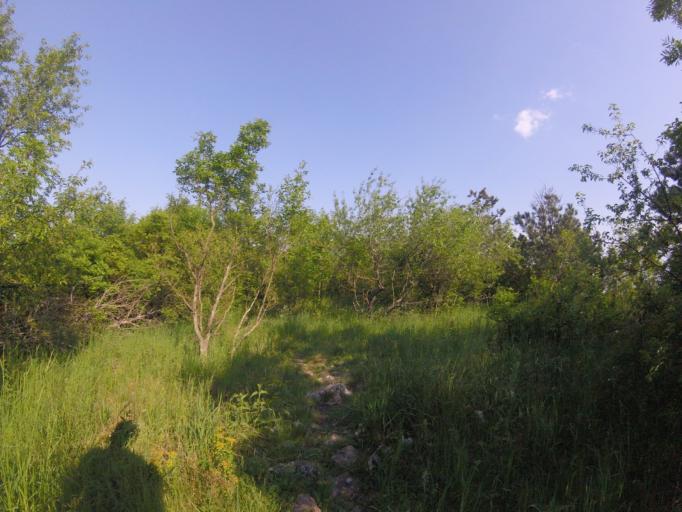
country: SK
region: Kosicky
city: Medzev
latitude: 48.6132
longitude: 20.8679
